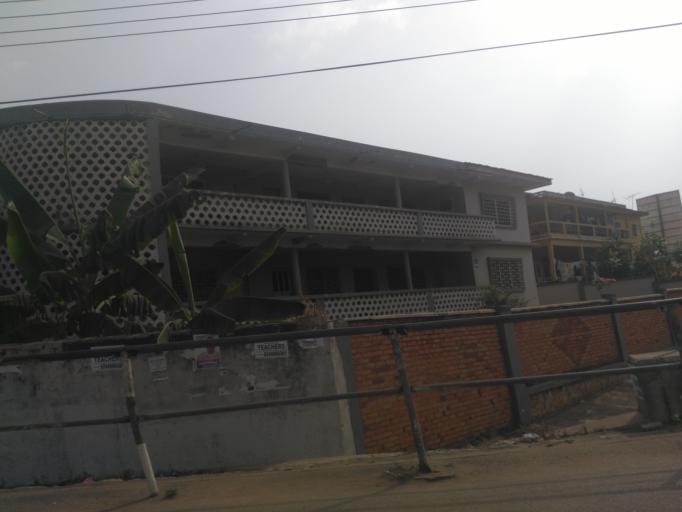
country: GH
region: Ashanti
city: Kumasi
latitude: 6.6892
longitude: -1.6034
